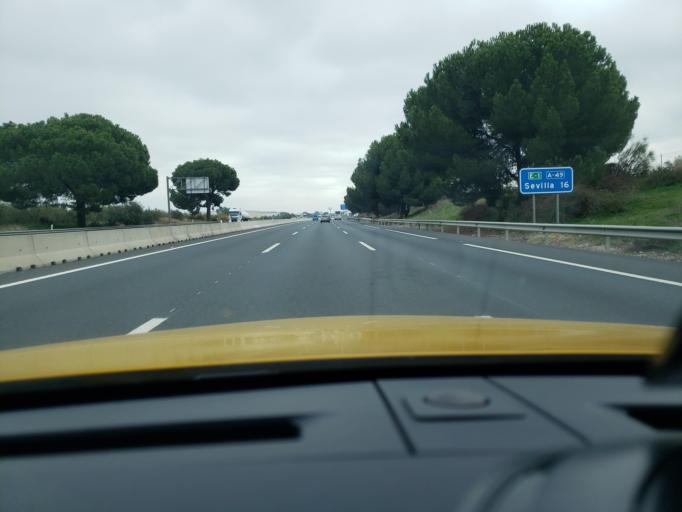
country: ES
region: Andalusia
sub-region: Provincia de Sevilla
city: Umbrete
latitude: 37.3580
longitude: -6.1605
